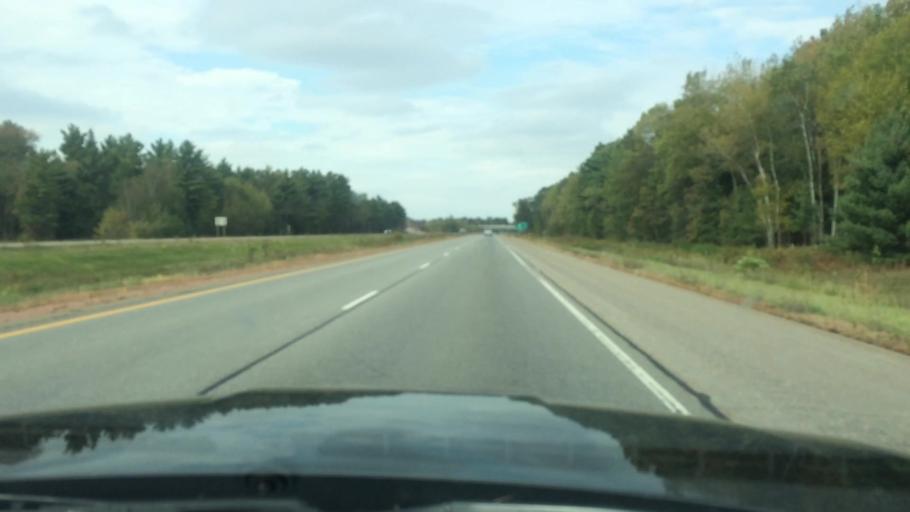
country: US
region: Wisconsin
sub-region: Marathon County
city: Mosinee
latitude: 44.7228
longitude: -89.6705
